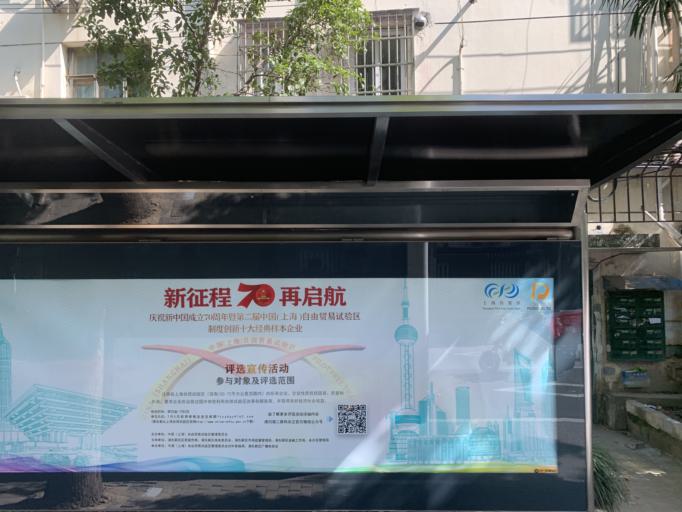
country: CN
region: Shanghai Shi
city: Pudong
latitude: 31.2354
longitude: 121.5204
